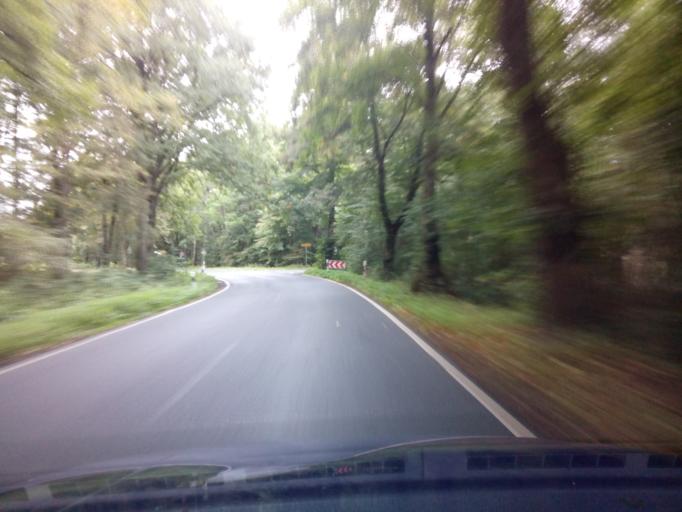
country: DE
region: Lower Saxony
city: Lubberstedt
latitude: 53.3567
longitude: 8.8266
